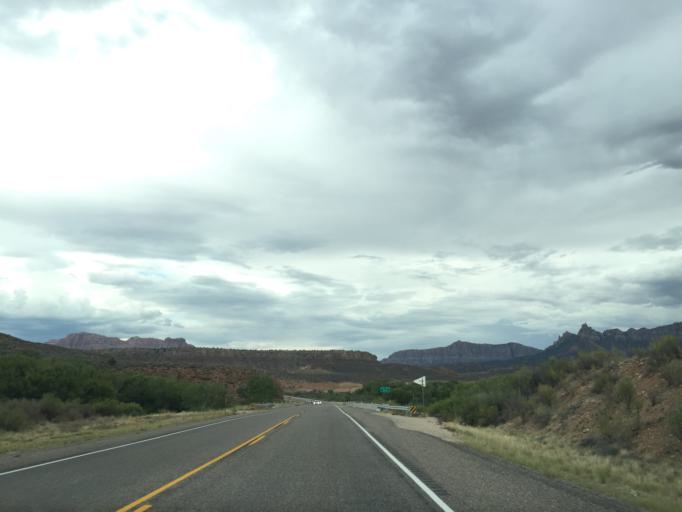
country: US
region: Utah
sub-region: Washington County
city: LaVerkin
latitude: 37.1710
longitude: -113.0846
